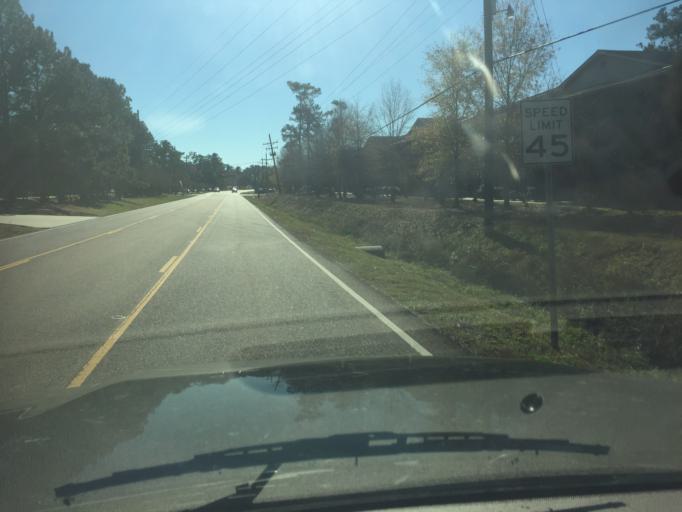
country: US
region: Louisiana
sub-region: Saint Tammany Parish
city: Slidell
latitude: 30.2990
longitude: -89.7229
